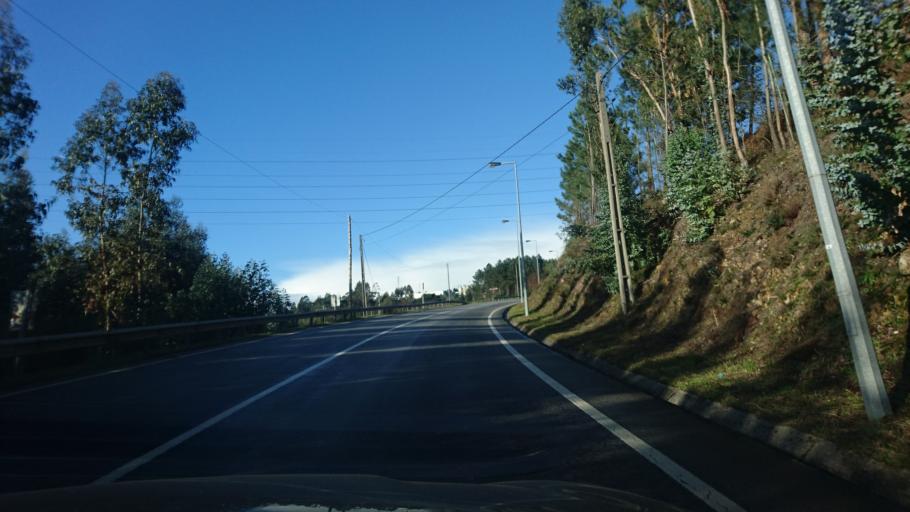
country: PT
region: Porto
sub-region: Paredes
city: Recarei
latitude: 41.1601
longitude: -8.4255
